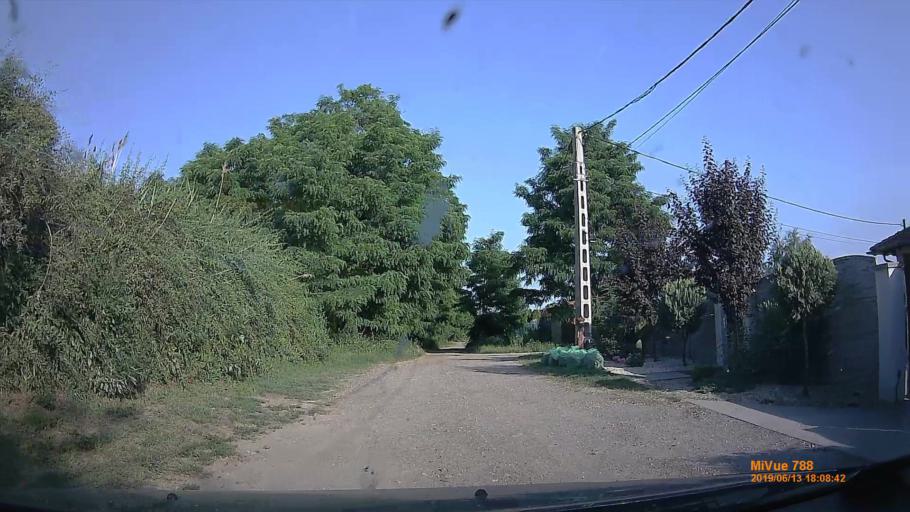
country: HU
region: Pest
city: Ecser
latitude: 47.4530
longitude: 19.3109
